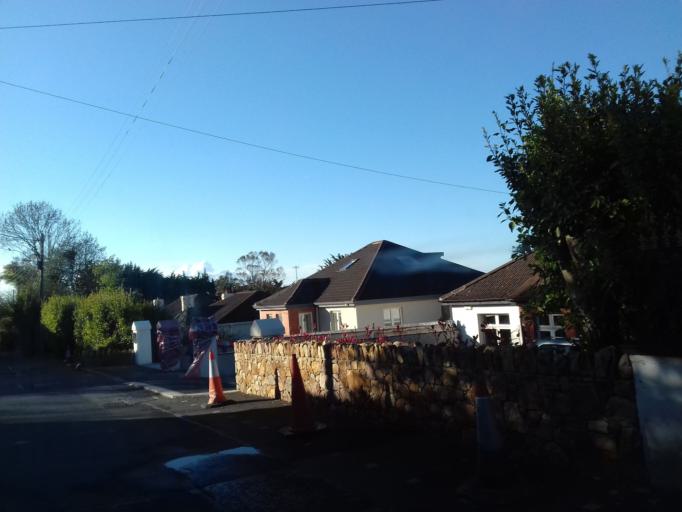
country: IE
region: Leinster
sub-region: Fingal County
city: Howth
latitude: 53.3765
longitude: -6.0630
